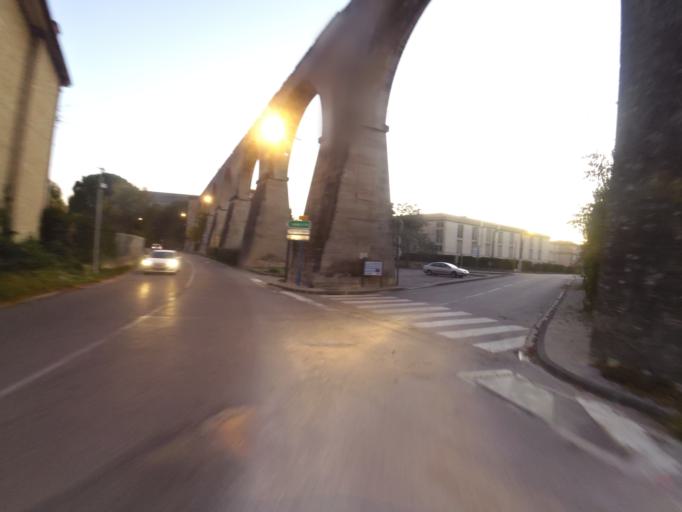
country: FR
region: Provence-Alpes-Cote d'Azur
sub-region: Departement du Vaucluse
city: Carpentras
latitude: 44.0613
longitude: 5.0586
